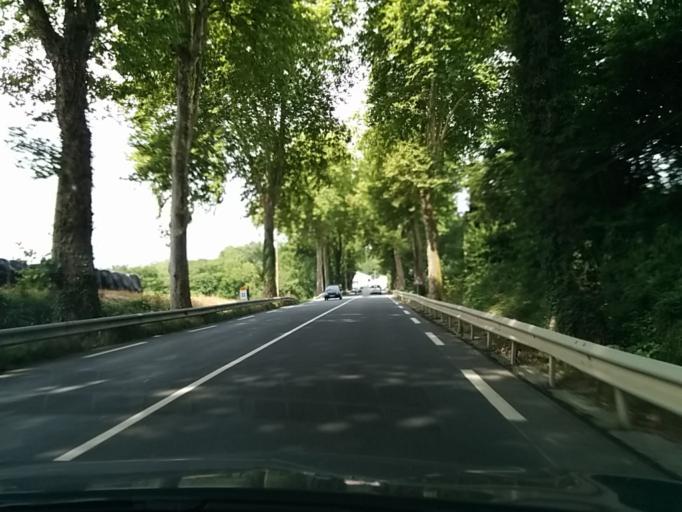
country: FR
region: Aquitaine
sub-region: Departement des Pyrenees-Atlantiques
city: Urrugne
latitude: 43.3619
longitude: -1.7144
